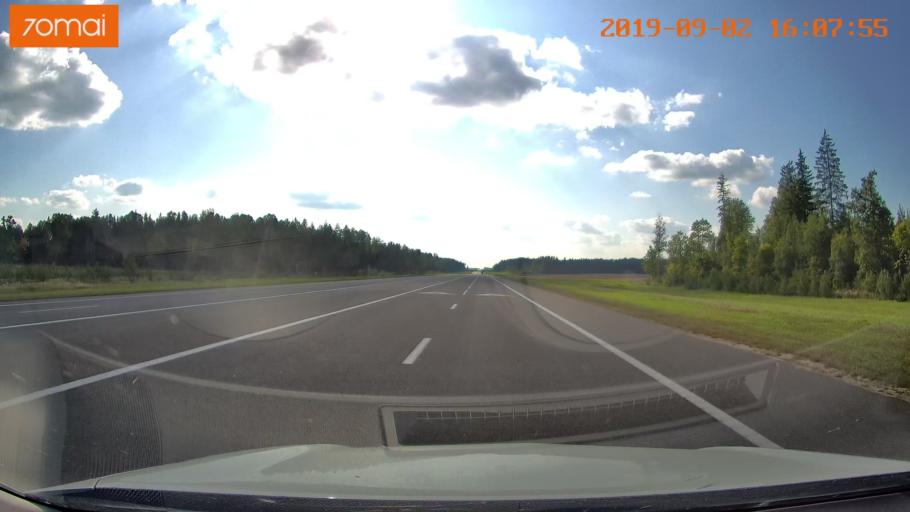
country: BY
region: Minsk
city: Byerazino
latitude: 53.7787
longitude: 28.7439
